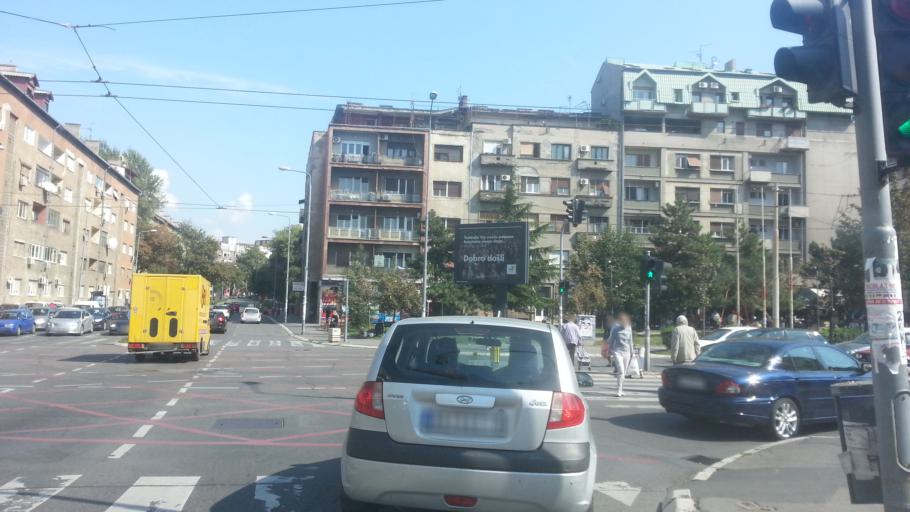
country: RS
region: Central Serbia
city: Belgrade
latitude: 44.8111
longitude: 20.4791
